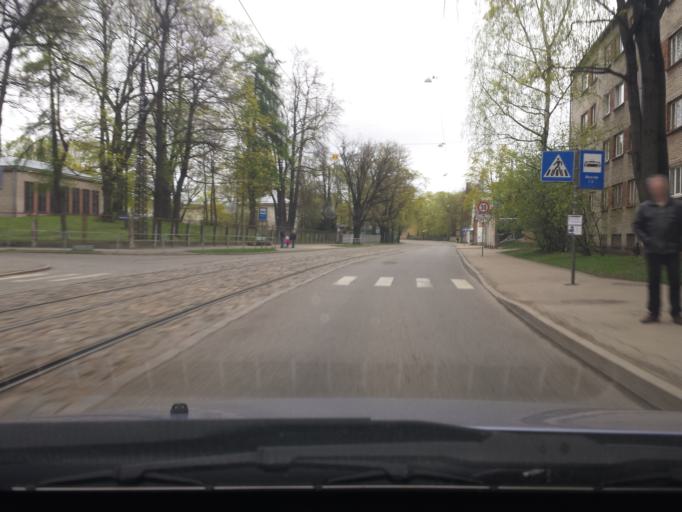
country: LV
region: Riga
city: Riga
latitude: 56.9530
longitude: 24.0629
